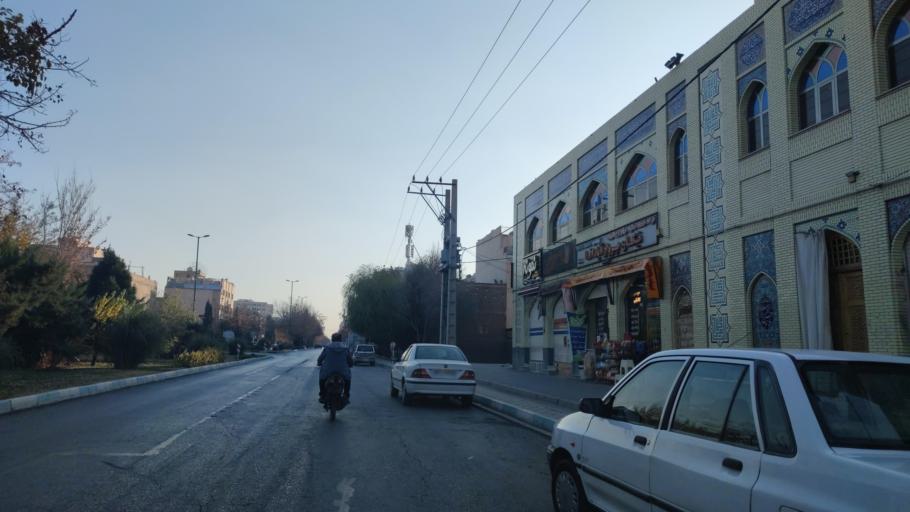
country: IR
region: Isfahan
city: Isfahan
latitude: 32.7077
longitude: 51.6803
